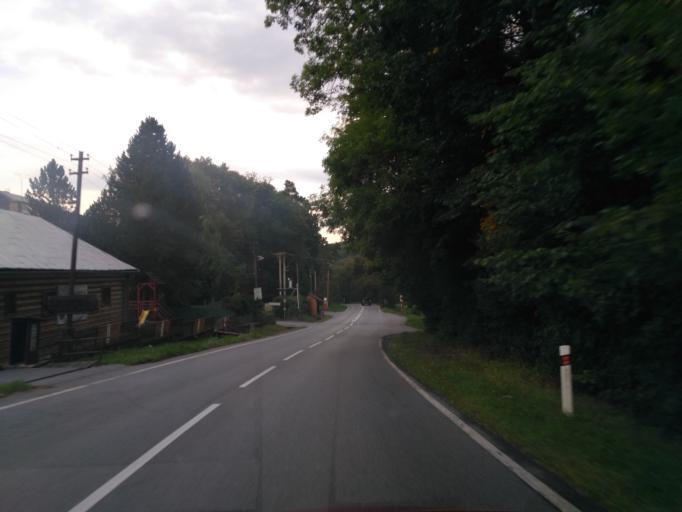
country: SK
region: Presovsky
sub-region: Okres Presov
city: Presov
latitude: 48.9883
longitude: 21.1769
